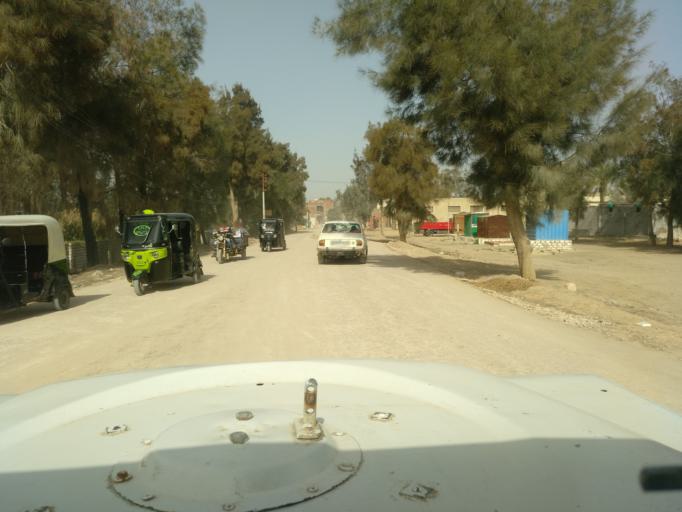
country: EG
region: Al Buhayrah
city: Beheira
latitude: 30.3691
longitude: 30.3577
